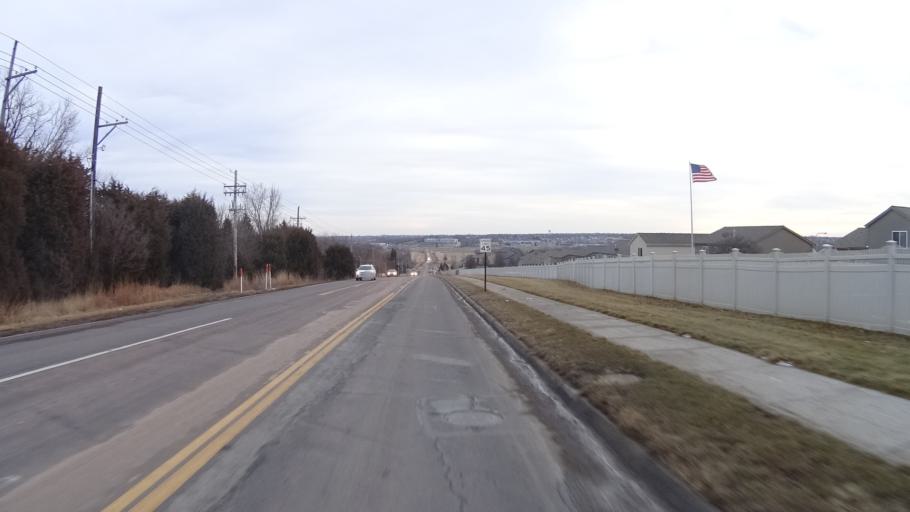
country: US
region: Nebraska
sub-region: Sarpy County
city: Offutt Air Force Base
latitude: 41.1543
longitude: -95.9477
